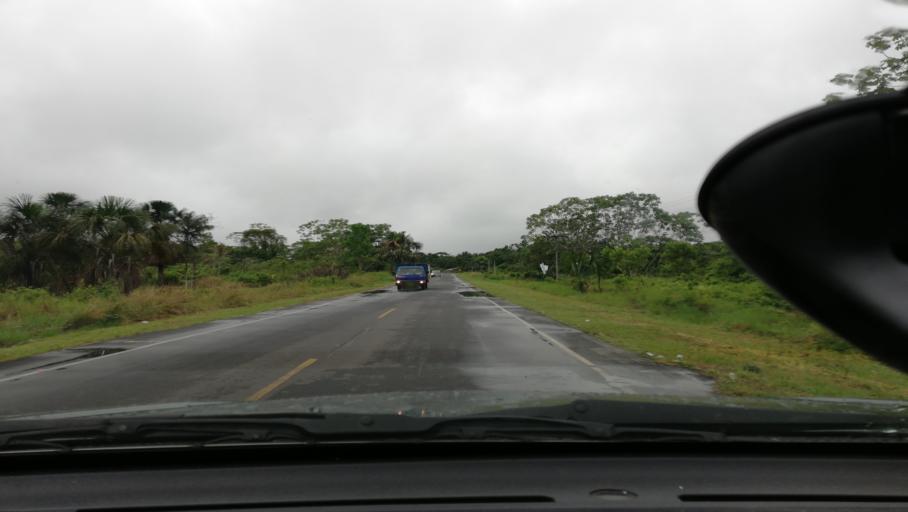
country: PE
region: Loreto
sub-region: Provincia de Maynas
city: San Juan
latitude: -4.0328
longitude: -73.4349
